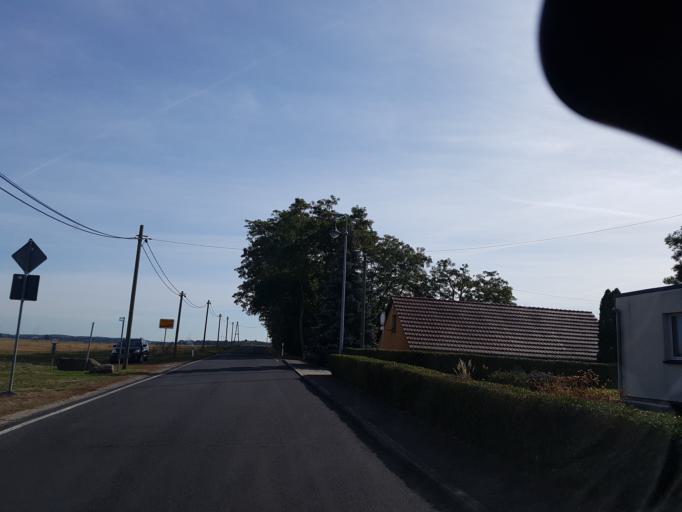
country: DE
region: Brandenburg
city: Schlieben
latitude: 51.7007
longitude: 13.4142
